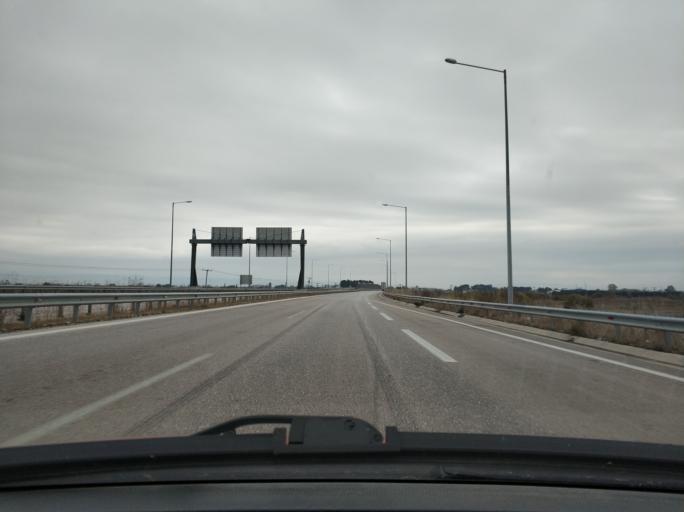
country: GR
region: Central Macedonia
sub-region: Nomos Thessalonikis
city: Lagyna
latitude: 40.7392
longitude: 23.0184
